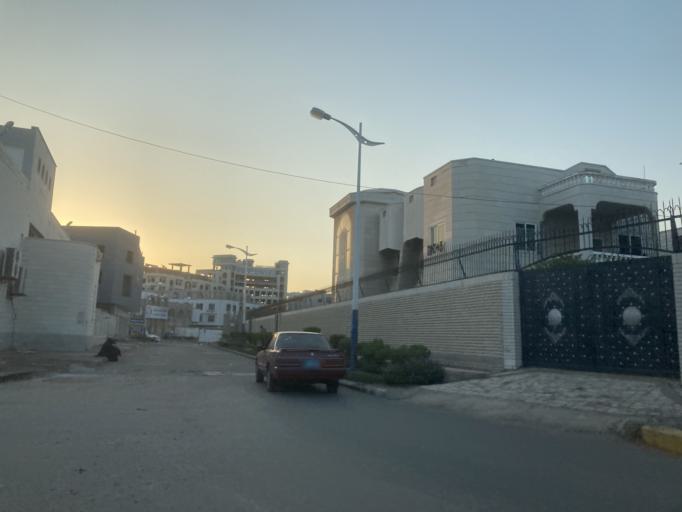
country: YE
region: Aden
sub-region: Al Mansura
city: Al Mansurah
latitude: 12.8516
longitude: 44.9910
